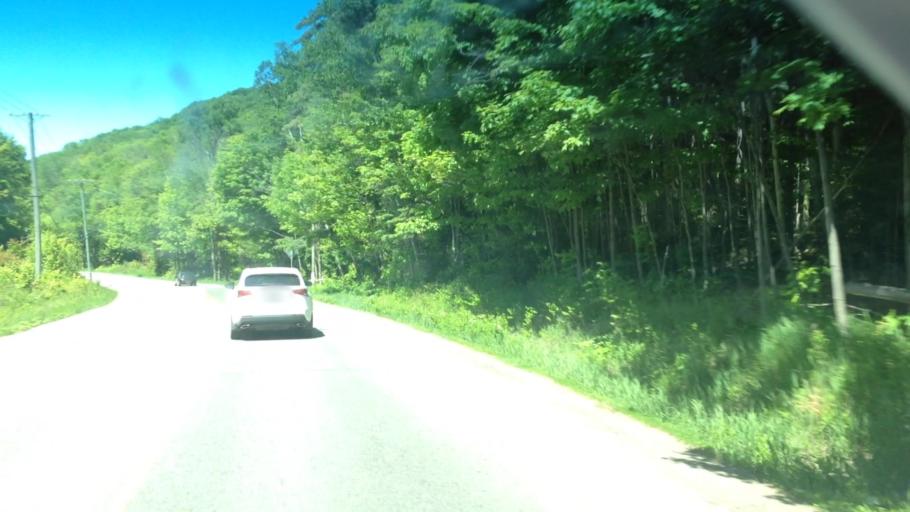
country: CA
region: Quebec
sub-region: Laurentides
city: Saint-Sauveur
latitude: 45.9108
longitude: -74.2692
